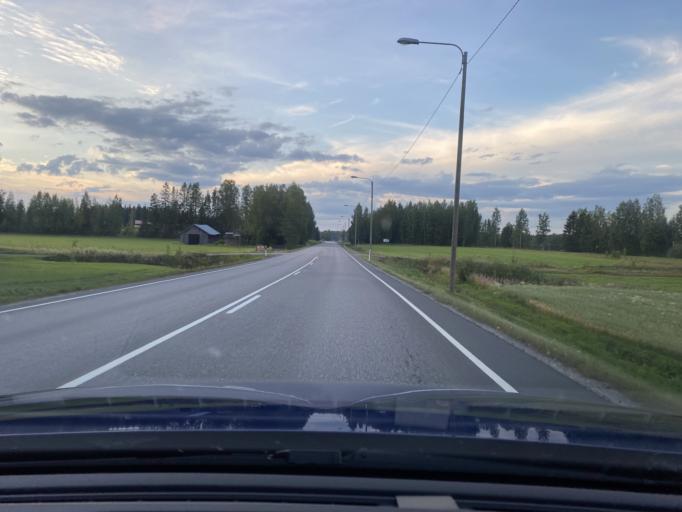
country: FI
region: Satakunta
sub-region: Pohjois-Satakunta
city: Kankaanpaeae
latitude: 61.7379
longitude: 22.5253
